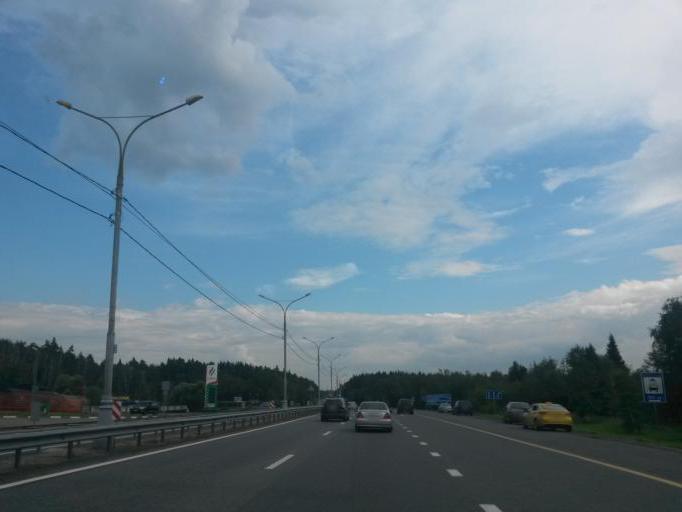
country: RU
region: Moskovskaya
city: Vostryakovo
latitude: 55.4536
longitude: 37.8569
